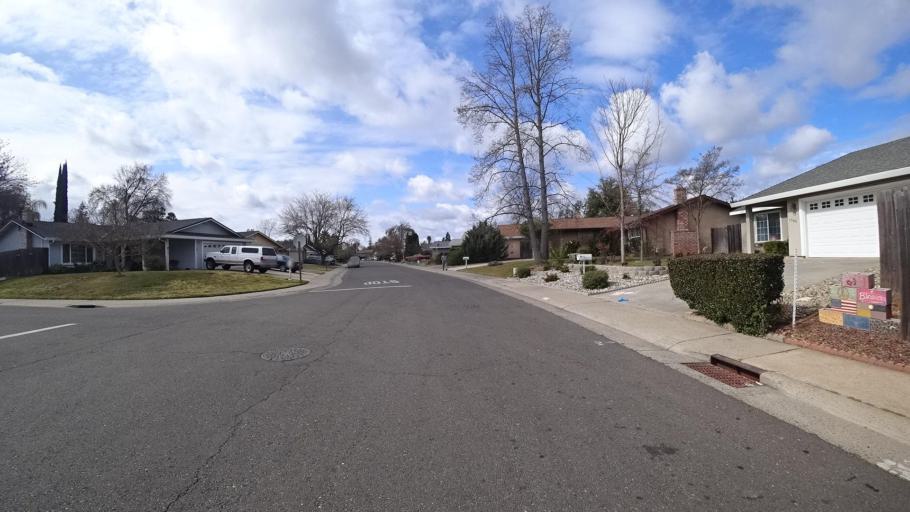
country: US
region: California
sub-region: Sacramento County
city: Fair Oaks
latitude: 38.6208
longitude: -121.2795
